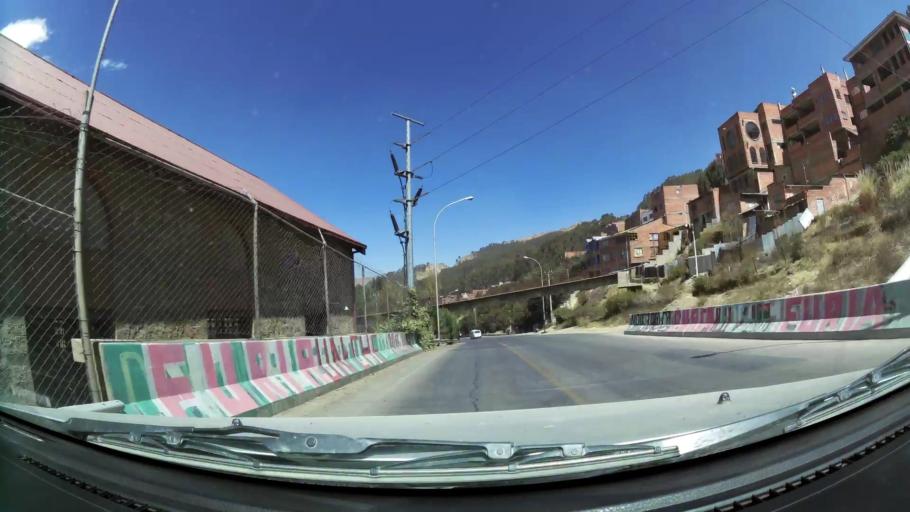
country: BO
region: La Paz
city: La Paz
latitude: -16.4657
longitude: -68.1527
